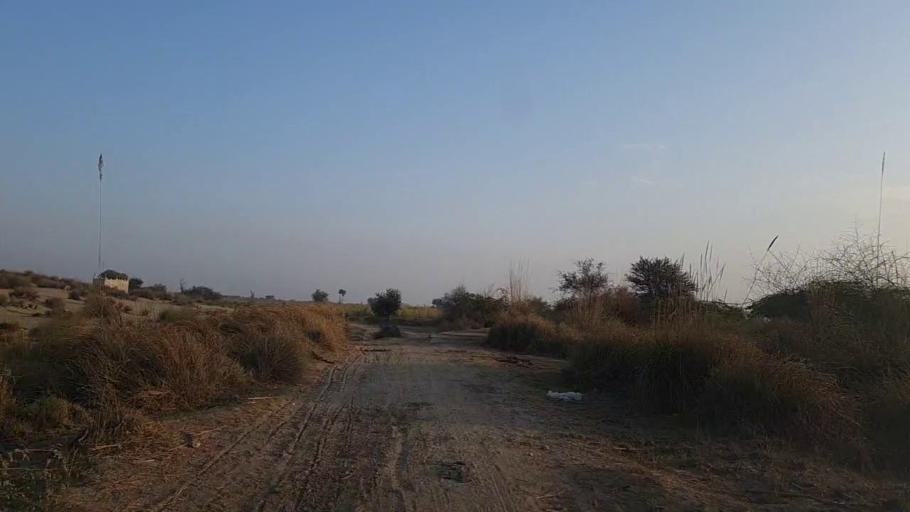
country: PK
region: Sindh
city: Daur
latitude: 26.4830
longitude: 68.4285
